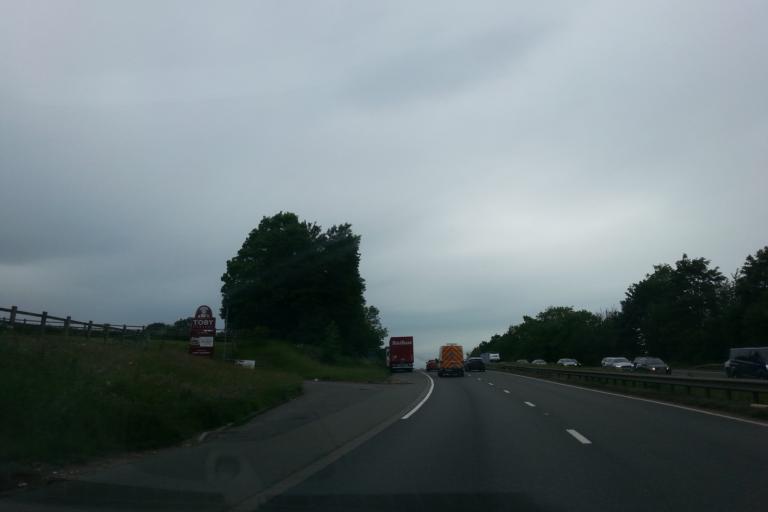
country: GB
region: England
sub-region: Solihull
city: Hampton in Arden
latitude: 52.4467
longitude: -1.6877
